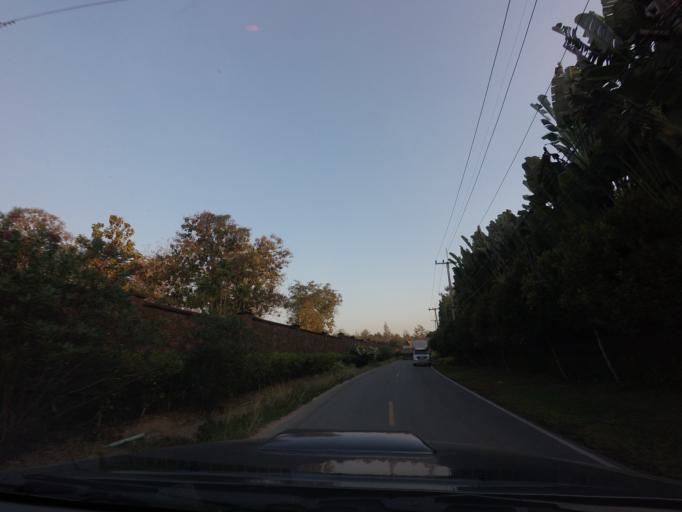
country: TH
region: Chiang Mai
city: Chiang Mai
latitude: 18.9227
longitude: 98.9103
